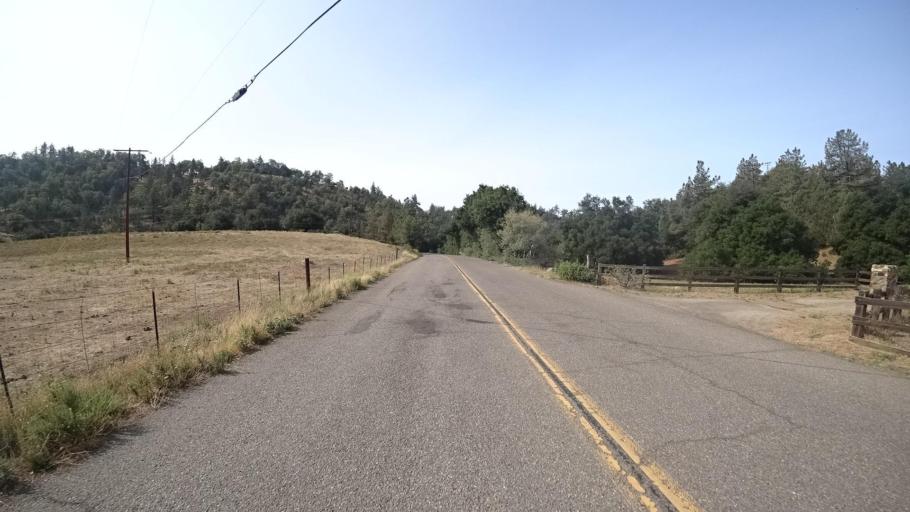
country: US
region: California
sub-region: San Diego County
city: Julian
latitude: 33.0986
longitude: -116.6135
